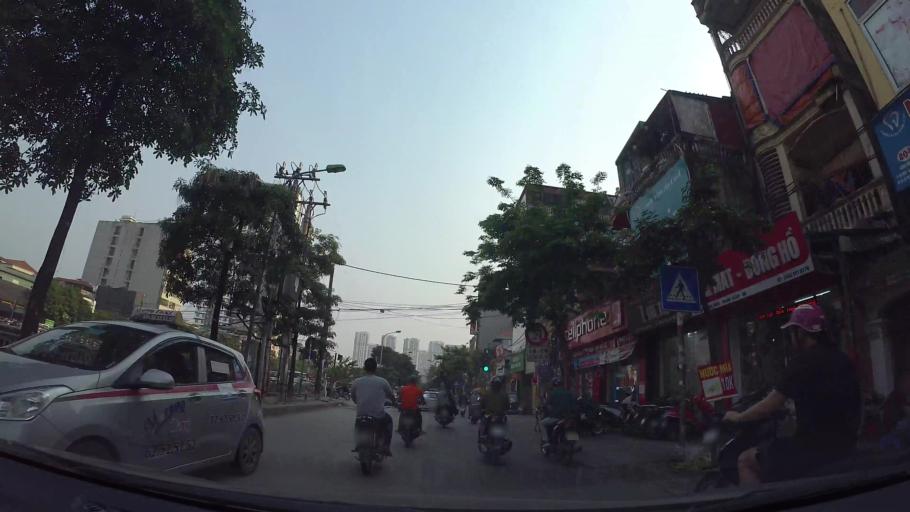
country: VN
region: Ha Noi
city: Thanh Xuan
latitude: 20.9932
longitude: 105.8139
